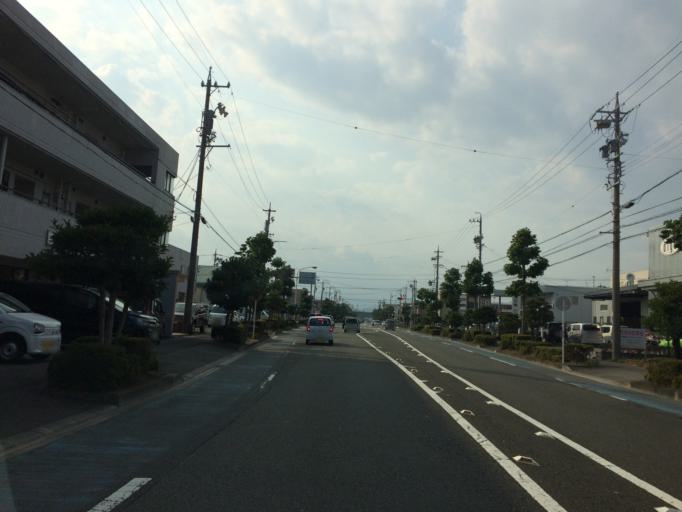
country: JP
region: Shizuoka
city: Shizuoka-shi
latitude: 34.9542
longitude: 138.4208
